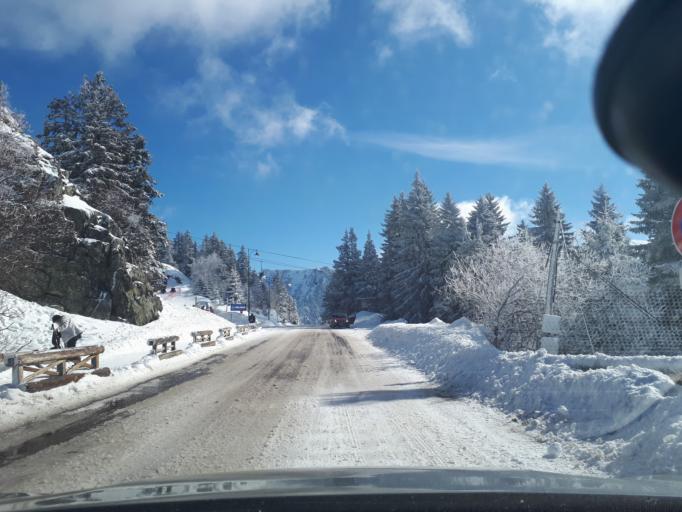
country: FR
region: Rhone-Alpes
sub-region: Departement de l'Isere
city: Vaulnaveys-le-Bas
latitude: 45.1048
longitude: 5.8764
